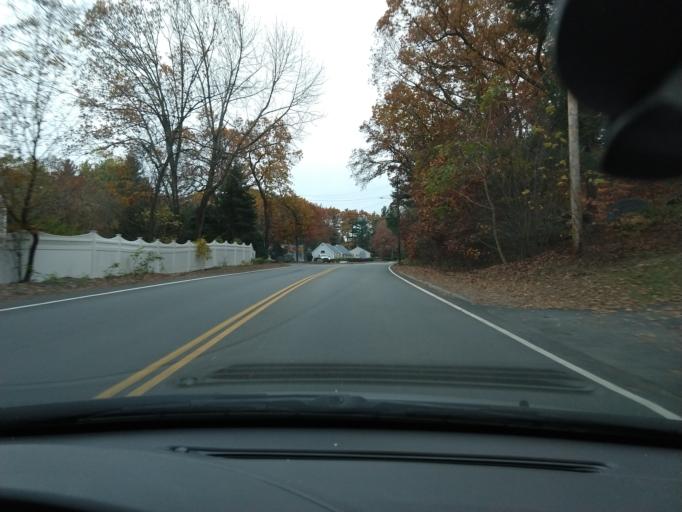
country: US
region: Massachusetts
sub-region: Middlesex County
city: Chelmsford
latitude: 42.5694
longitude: -71.3501
